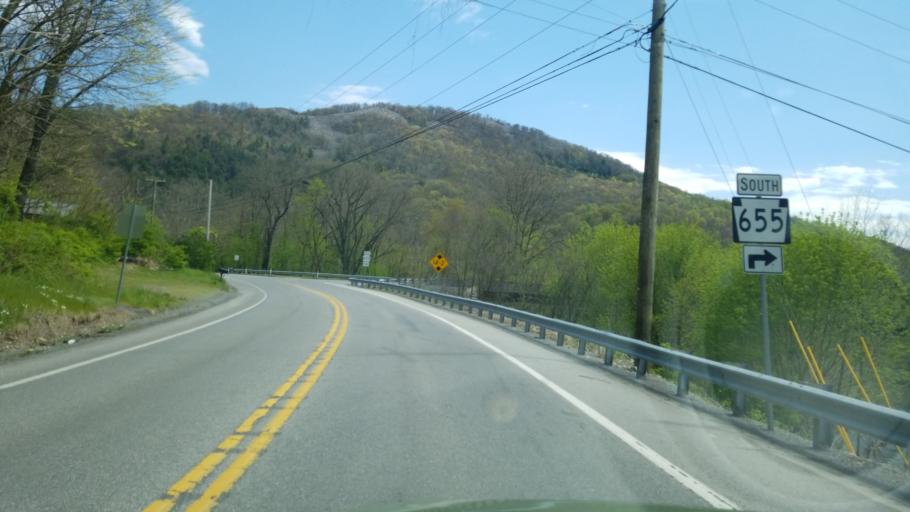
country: US
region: Pennsylvania
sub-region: Huntingdon County
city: Mount Union
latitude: 40.3956
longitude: -77.9395
